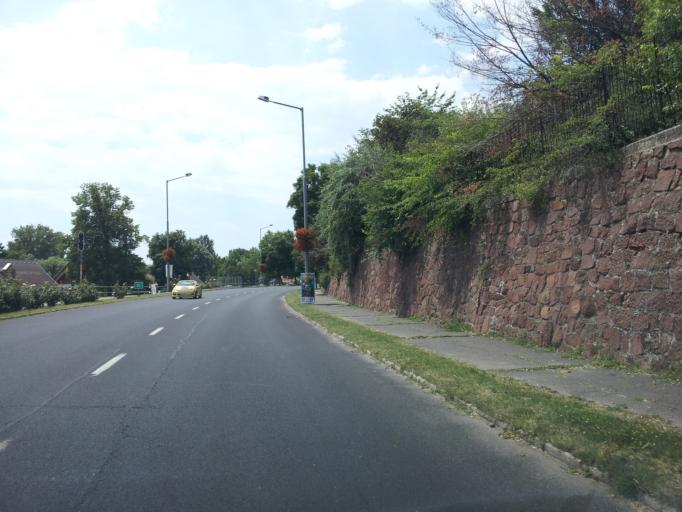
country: HU
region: Veszprem
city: Balatonalmadi
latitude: 46.9871
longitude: 17.9841
